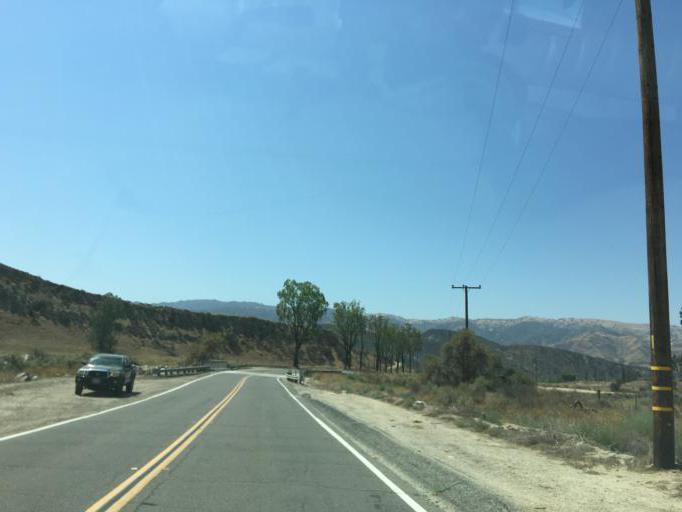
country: US
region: California
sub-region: Los Angeles County
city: Val Verde
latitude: 34.4247
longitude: -118.6573
